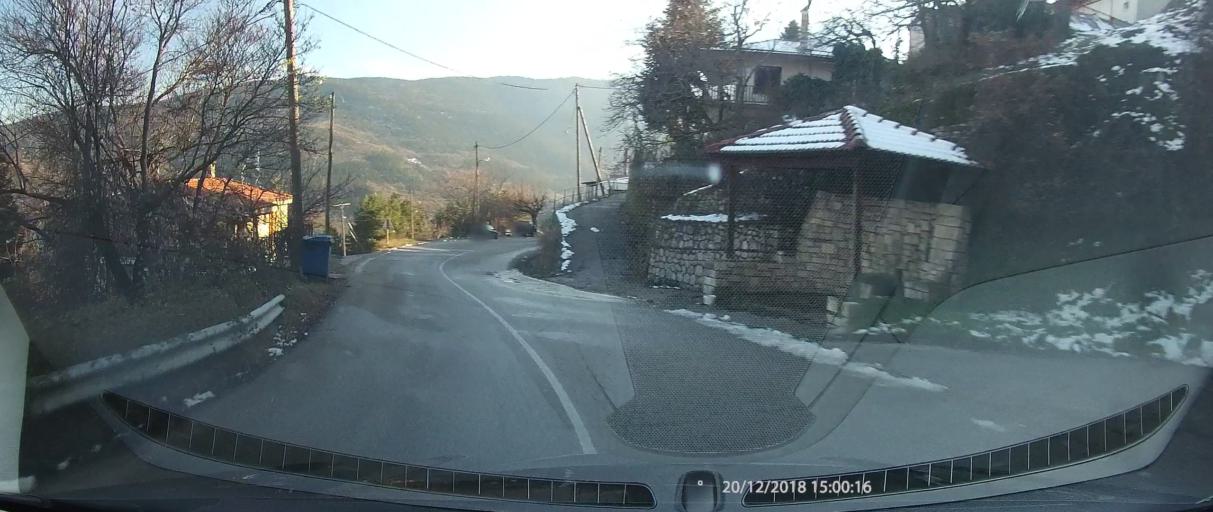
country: GR
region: Central Greece
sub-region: Nomos Evrytanias
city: Karpenisi
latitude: 38.9089
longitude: 21.9166
